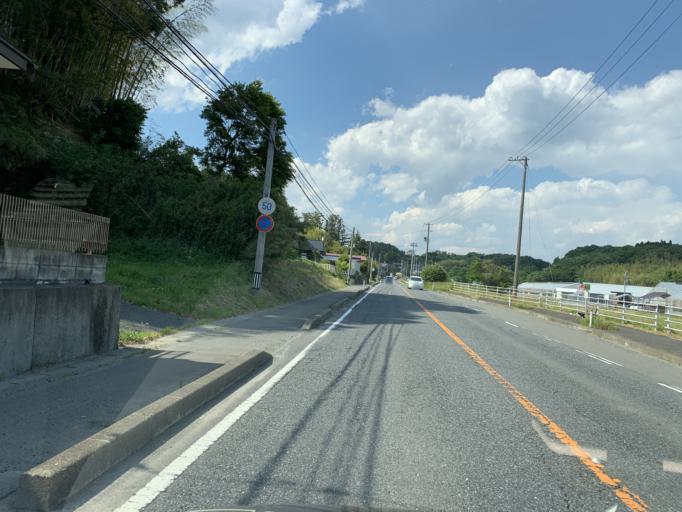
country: JP
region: Miyagi
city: Wakuya
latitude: 38.4857
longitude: 141.1080
